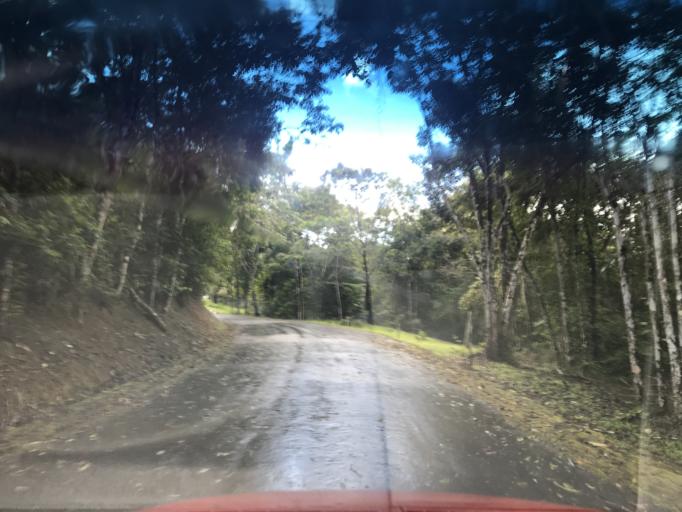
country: BR
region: Bahia
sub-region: Gandu
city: Gandu
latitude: -13.9000
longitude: -39.4596
